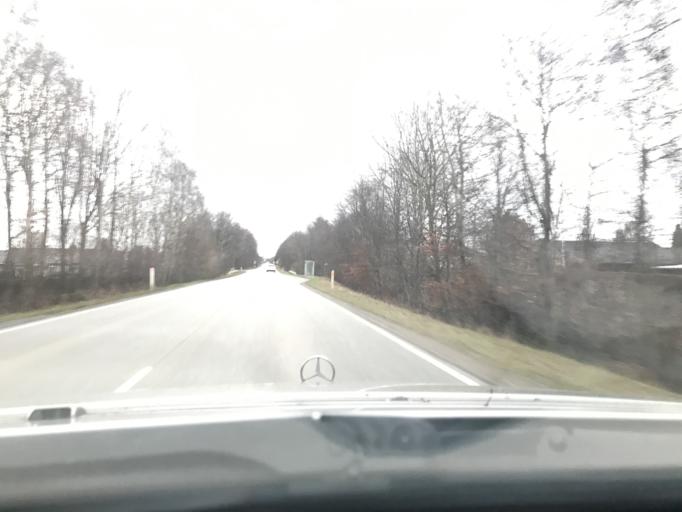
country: DK
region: South Denmark
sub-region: Aabenraa Kommune
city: Rodekro
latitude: 55.0741
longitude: 9.3145
